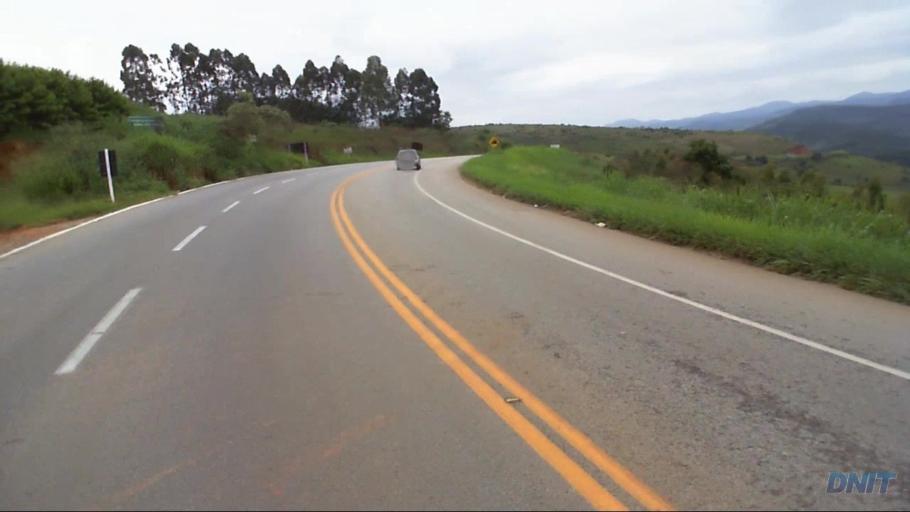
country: BR
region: Minas Gerais
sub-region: Nova Era
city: Nova Era
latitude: -19.8072
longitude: -43.0644
